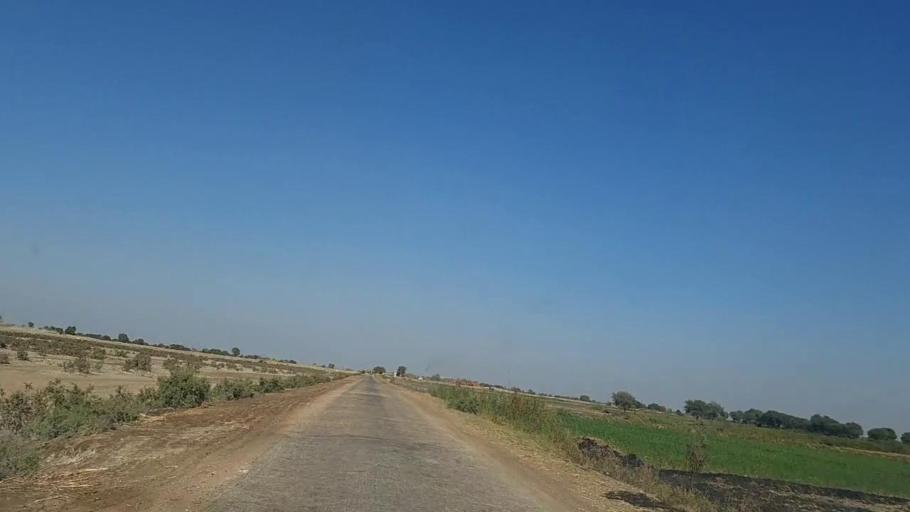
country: PK
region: Sindh
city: Digri
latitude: 25.1491
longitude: 69.0184
